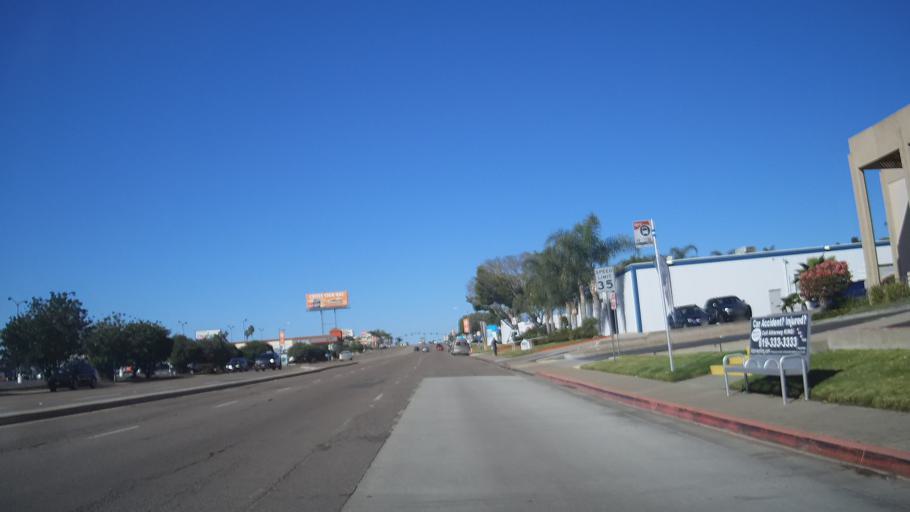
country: US
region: California
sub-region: San Diego County
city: San Diego
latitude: 32.8329
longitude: -117.1537
